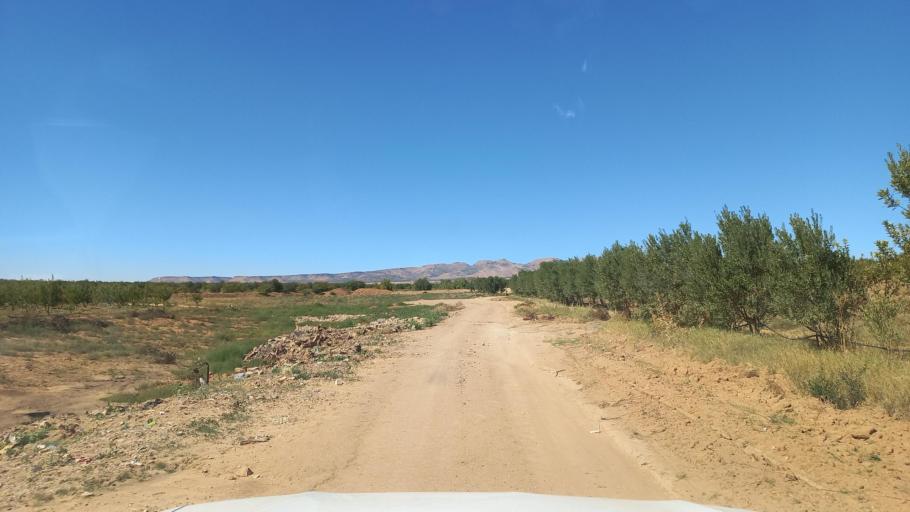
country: TN
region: Al Qasrayn
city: Sbiba
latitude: 35.3614
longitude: 9.0841
